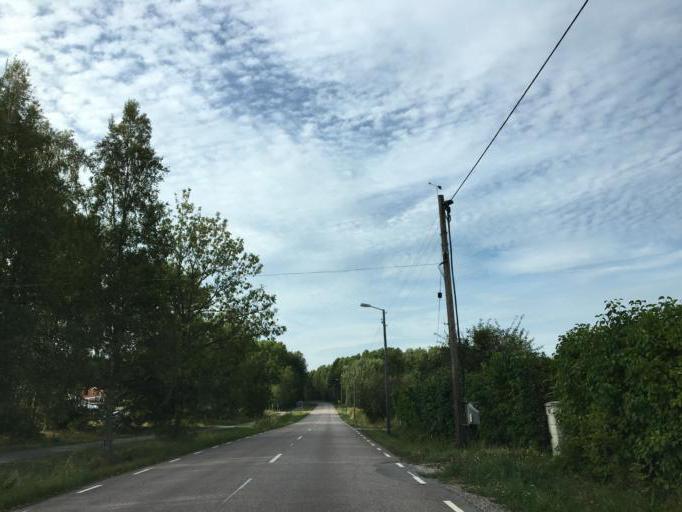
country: SE
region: Soedermanland
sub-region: Eskilstuna Kommun
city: Torshalla
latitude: 59.4447
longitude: 16.4507
